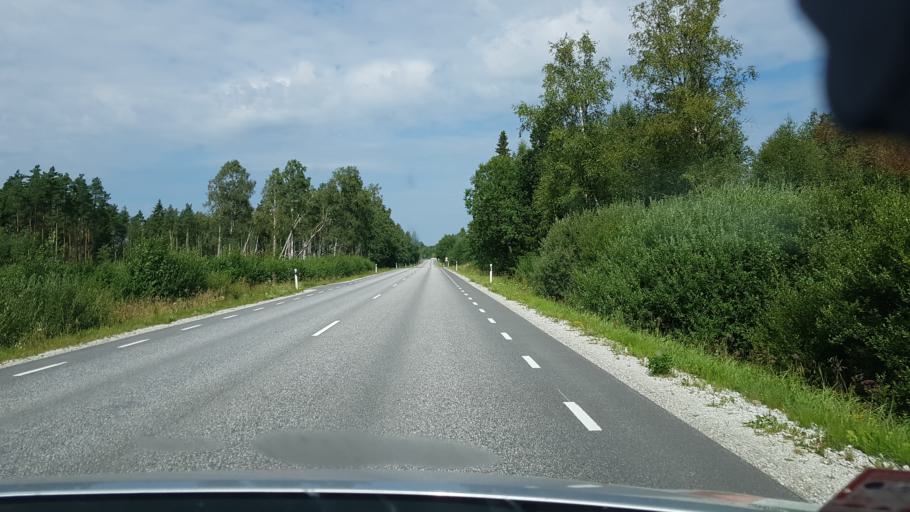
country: EE
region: Raplamaa
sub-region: Jaervakandi vald
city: Jarvakandi
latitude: 58.8692
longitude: 24.7838
